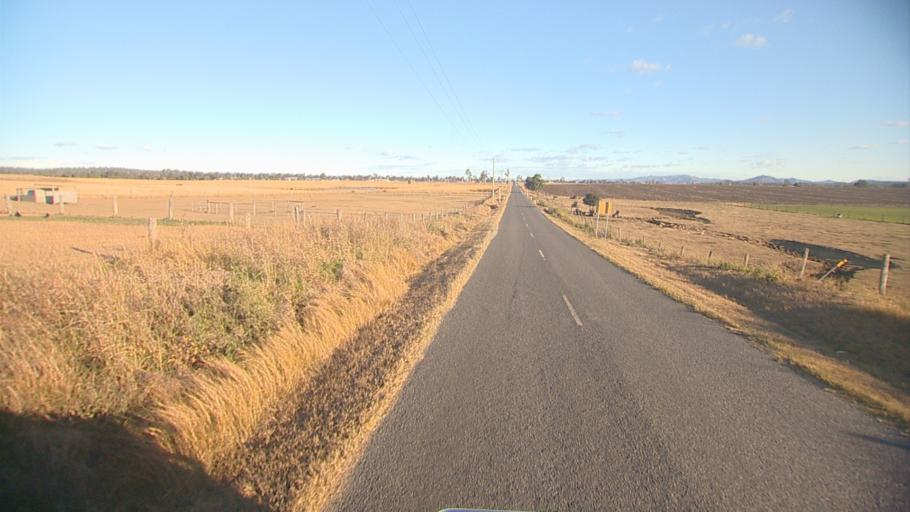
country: AU
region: Queensland
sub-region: Logan
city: Cedar Vale
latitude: -27.8601
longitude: 152.9591
